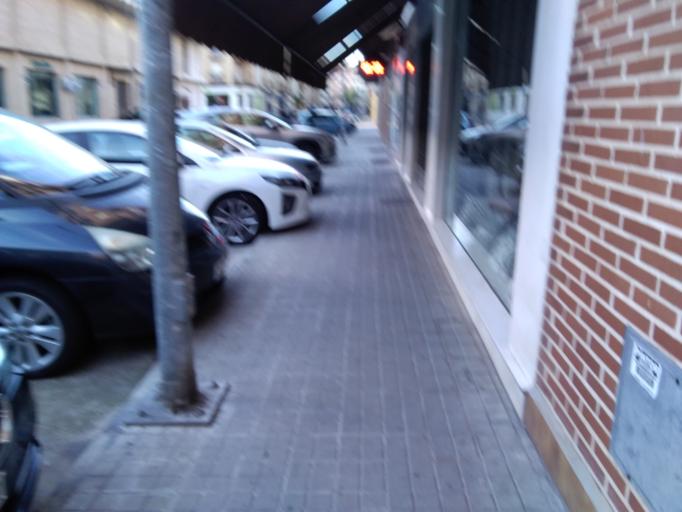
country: ES
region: Castille-La Mancha
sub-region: Province of Toledo
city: Toledo
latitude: 39.8688
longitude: -4.0328
